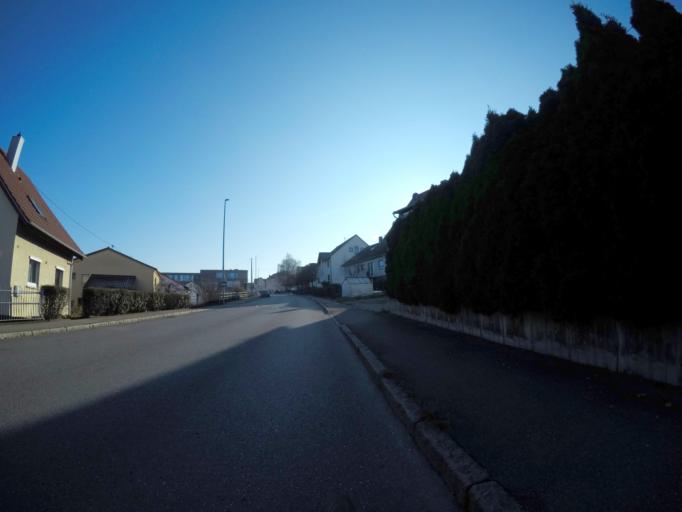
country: DE
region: Baden-Wuerttemberg
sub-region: Tuebingen Region
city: Reutlingen
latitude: 48.5218
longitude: 9.2269
